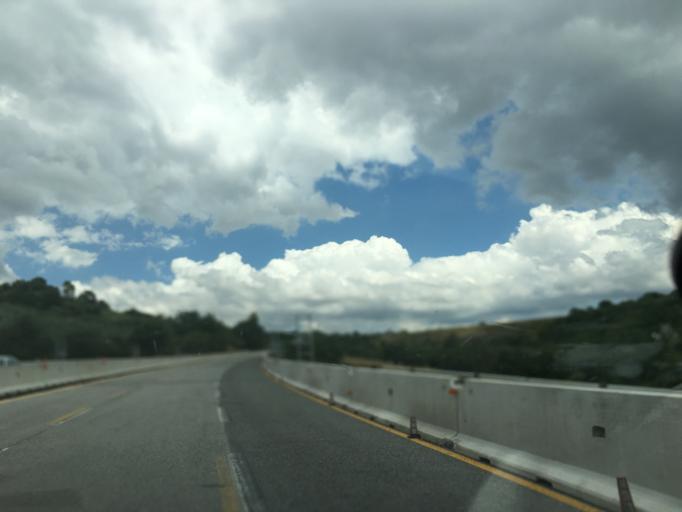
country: IT
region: Campania
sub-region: Provincia di Avellino
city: Bonito
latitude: 41.0724
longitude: 14.9785
